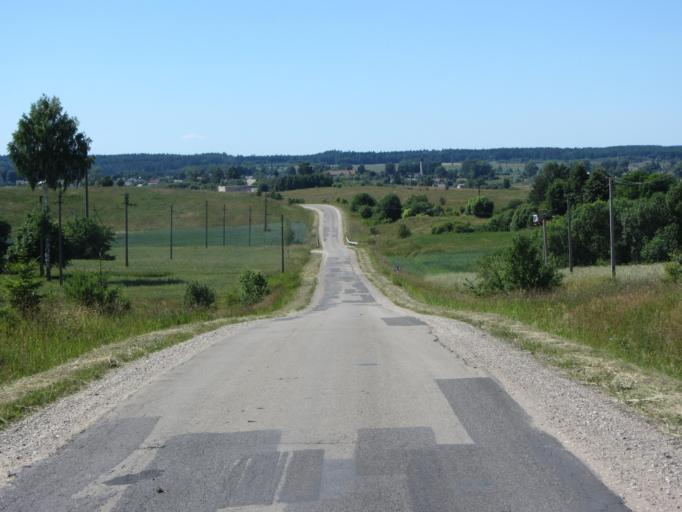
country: LT
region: Vilnius County
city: Elektrenai
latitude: 54.7111
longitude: 24.6983
